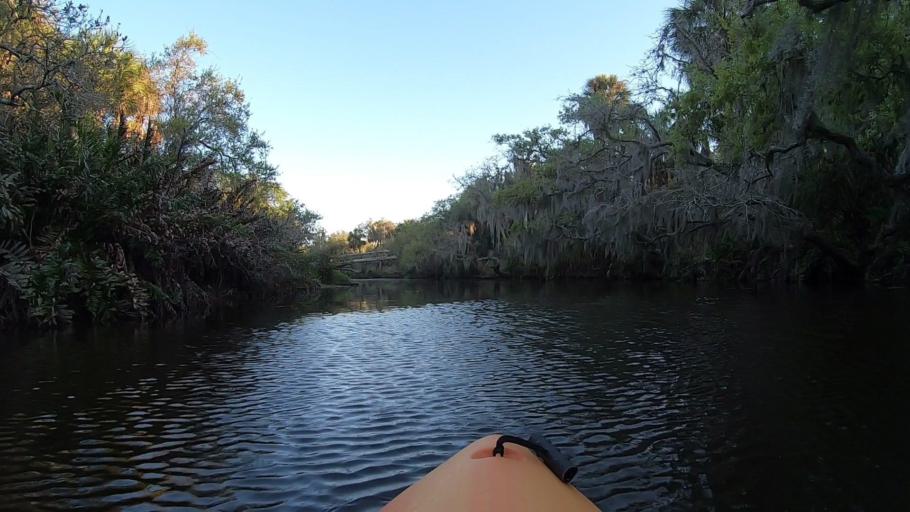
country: US
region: Florida
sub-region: Manatee County
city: Memphis
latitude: 27.5911
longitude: -82.5552
